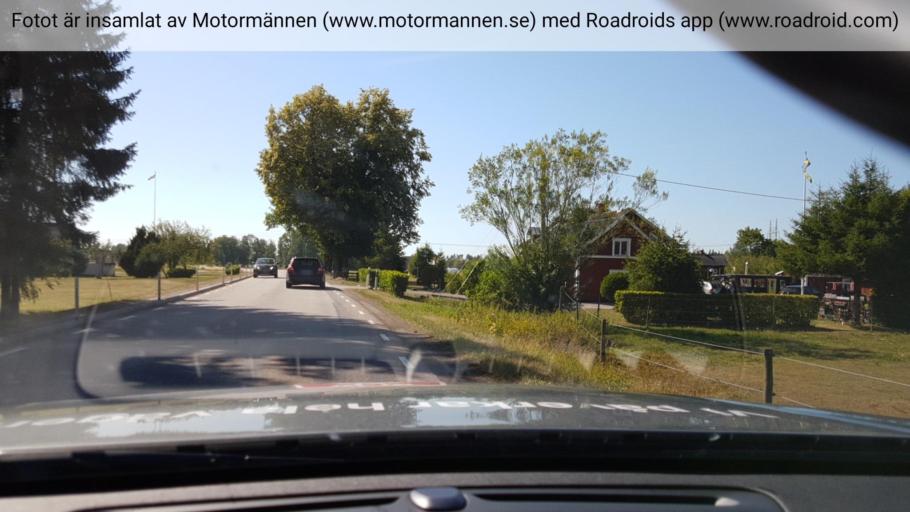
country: SE
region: Vaestra Goetaland
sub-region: Toreboda Kommun
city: Toereboda
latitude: 58.7084
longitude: 14.1718
